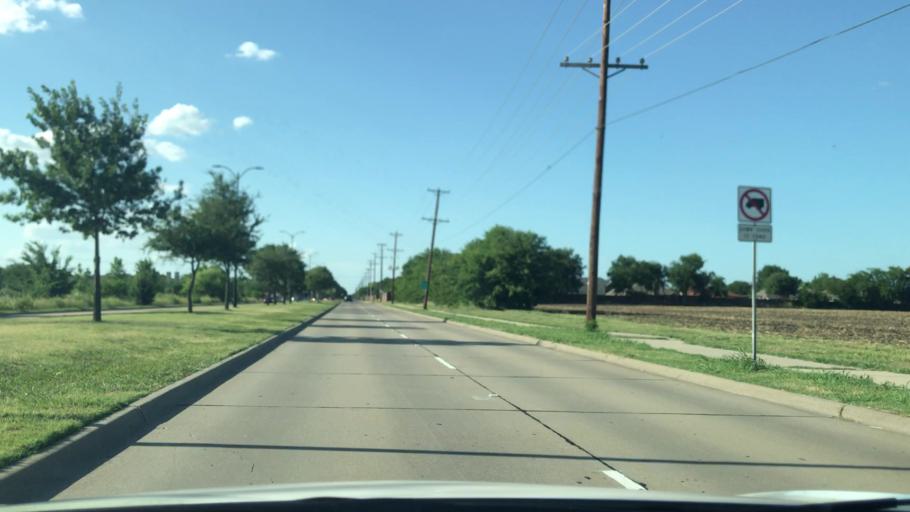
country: US
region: Texas
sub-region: Collin County
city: Frisco
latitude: 33.1061
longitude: -96.7882
